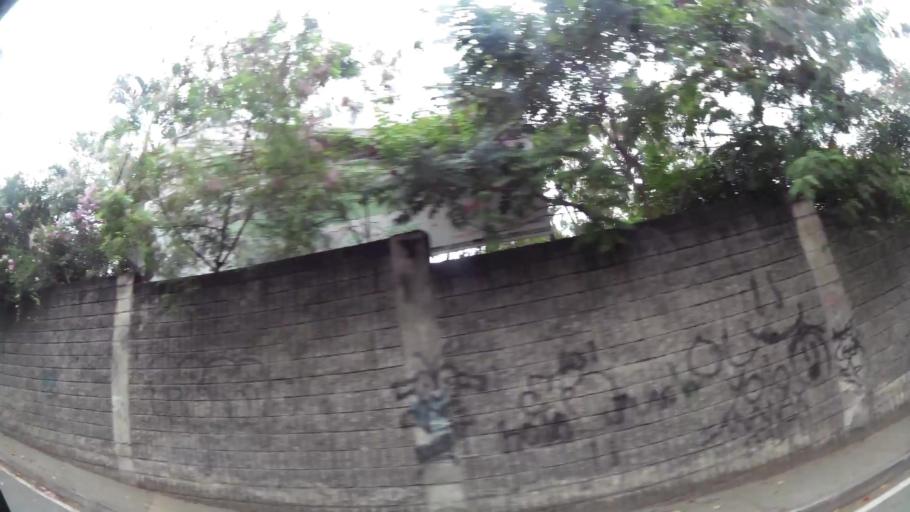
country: CO
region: Antioquia
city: Medellin
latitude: 6.2784
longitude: -75.5930
